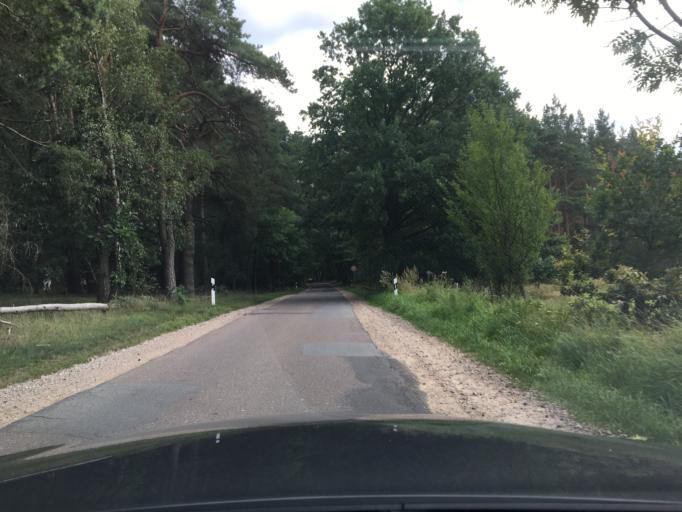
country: DE
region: Mecklenburg-Vorpommern
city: Waren
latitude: 53.4780
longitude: 12.7740
